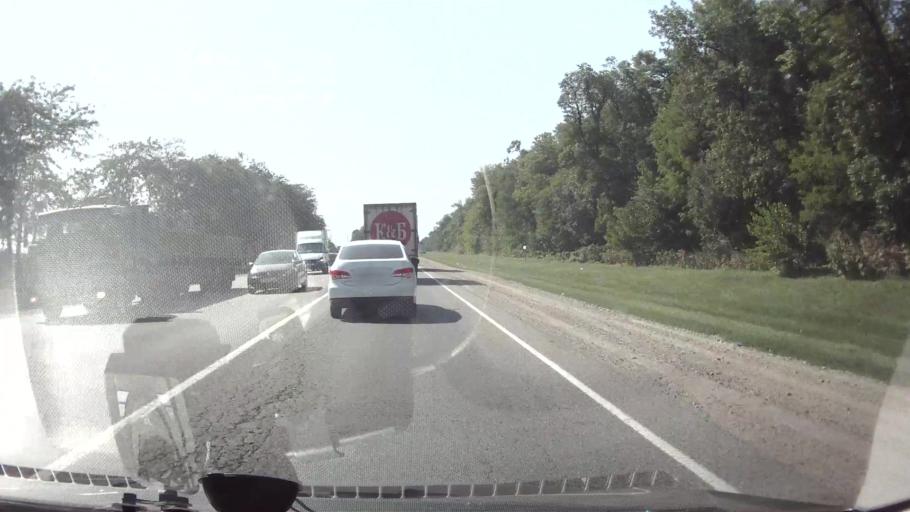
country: RU
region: Krasnodarskiy
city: Starokorsunskaya
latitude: 45.0333
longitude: 39.2384
